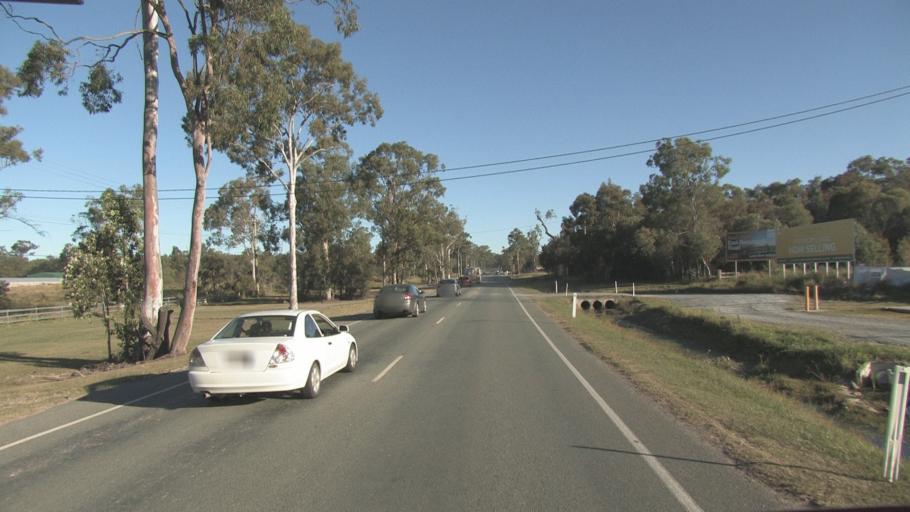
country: AU
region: Queensland
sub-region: Logan
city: Logan Reserve
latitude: -27.7151
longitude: 153.0925
